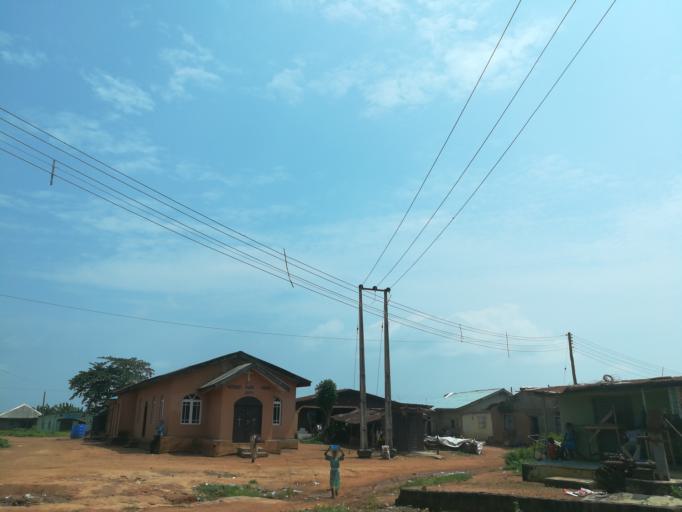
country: NG
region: Lagos
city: Ikorodu
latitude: 6.5749
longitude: 3.6296
